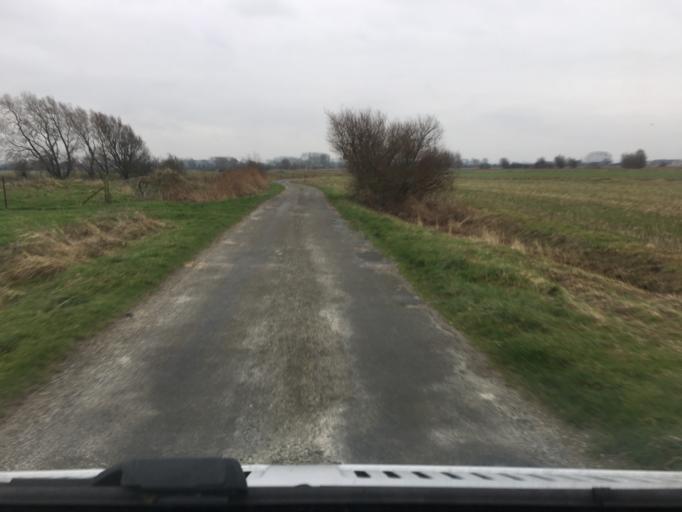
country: FR
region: Picardie
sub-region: Departement de la Somme
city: Pende
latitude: 50.1814
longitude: 1.5447
